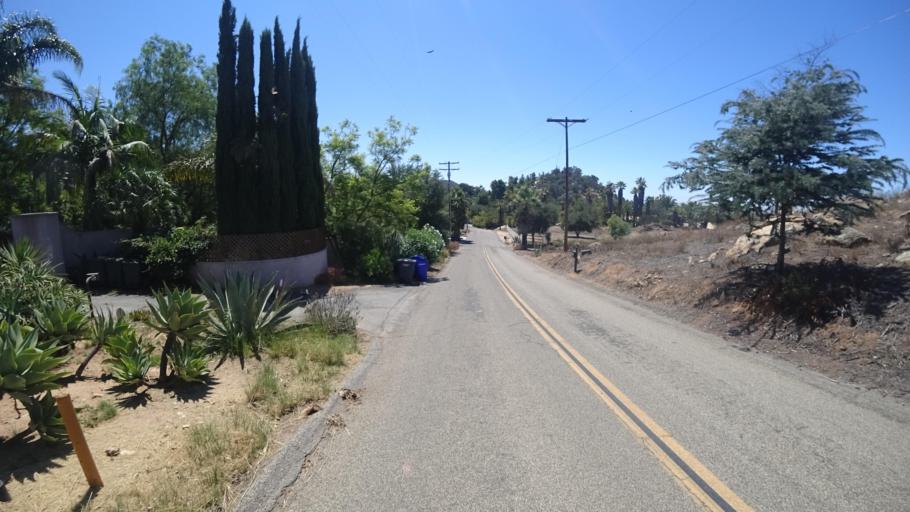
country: US
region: California
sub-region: San Diego County
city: Rainbow
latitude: 33.3894
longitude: -117.1305
